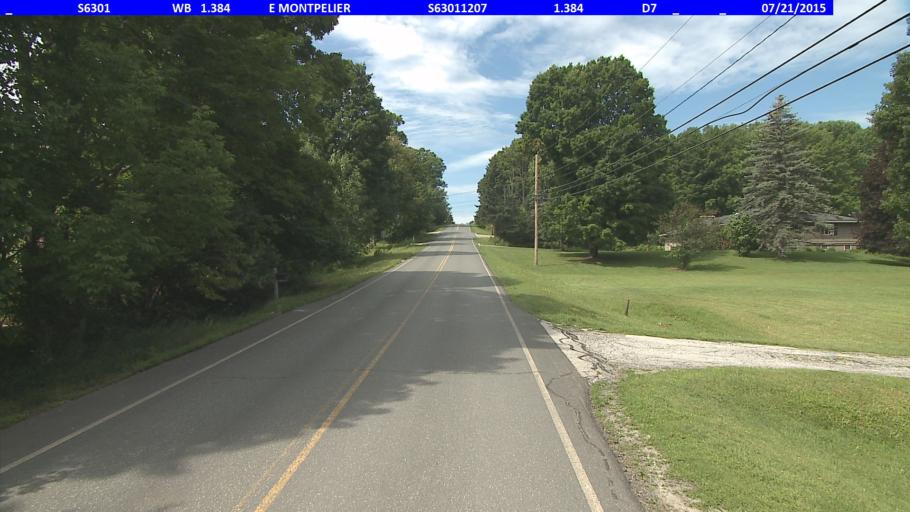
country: US
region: Vermont
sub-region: Washington County
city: Montpelier
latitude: 44.2833
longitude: -72.5302
